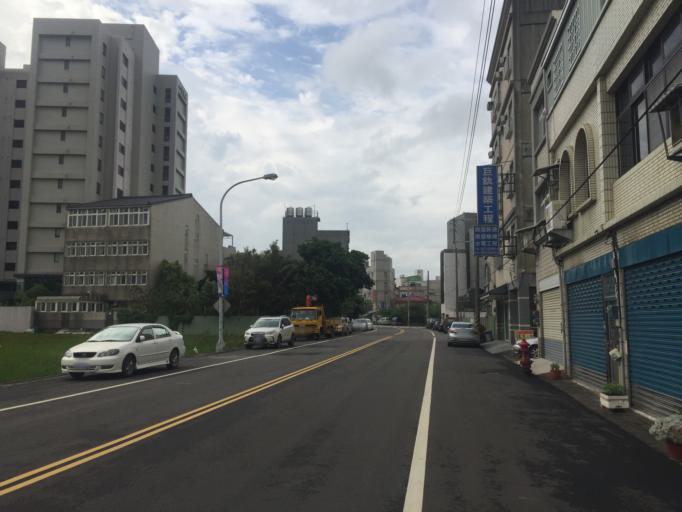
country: TW
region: Taiwan
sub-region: Hsinchu
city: Hsinchu
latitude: 24.6969
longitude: 120.8932
